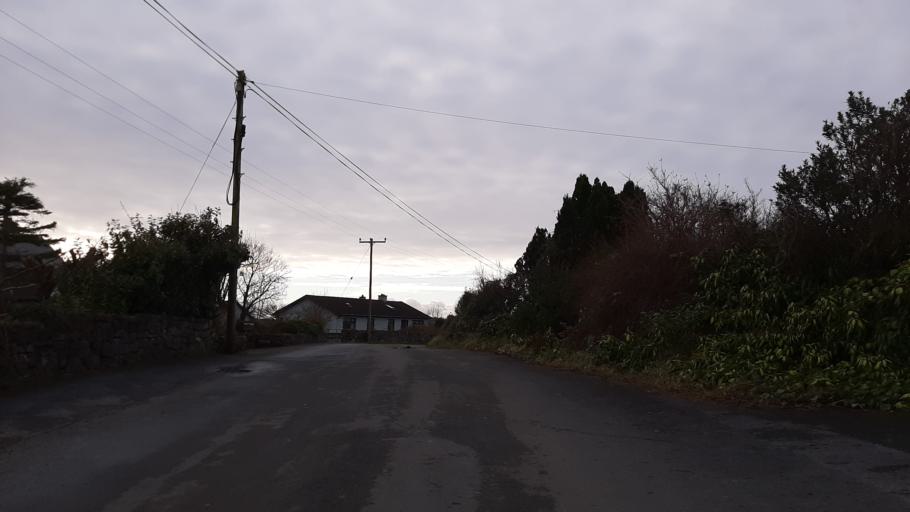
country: IE
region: Connaught
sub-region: County Galway
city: Gaillimh
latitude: 53.3071
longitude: -9.0694
